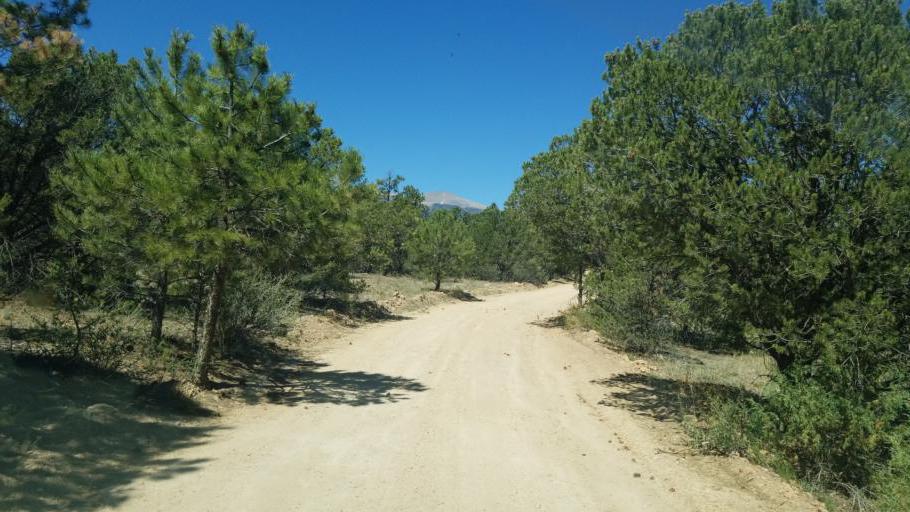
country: US
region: Colorado
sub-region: Custer County
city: Westcliffe
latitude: 38.2527
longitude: -105.5638
